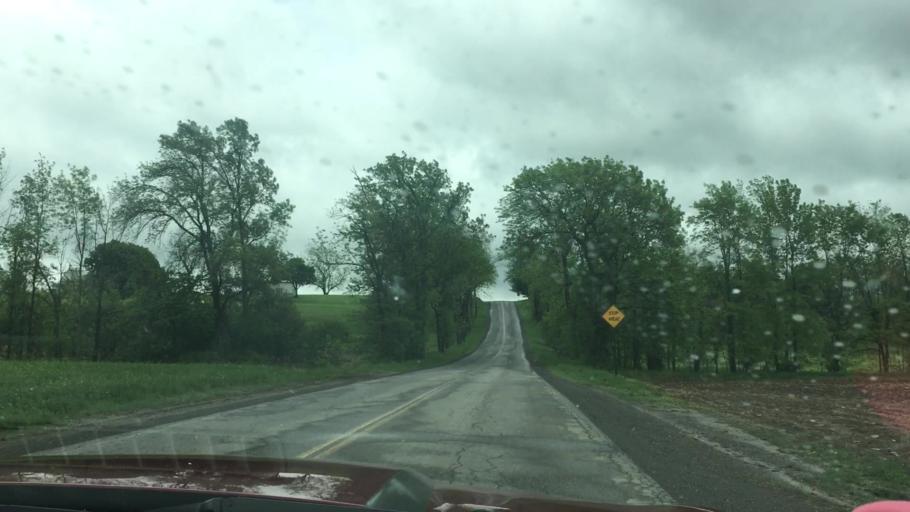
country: US
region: New York
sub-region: Genesee County
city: Batavia
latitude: 43.0865
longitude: -78.1393
